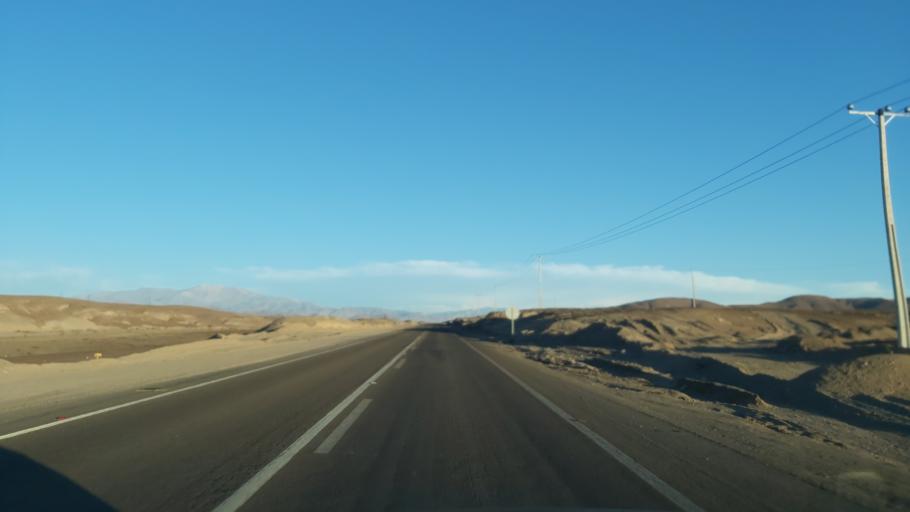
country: CL
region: Atacama
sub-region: Provincia de Chanaral
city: Diego de Almagro
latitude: -26.4271
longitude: -70.0162
